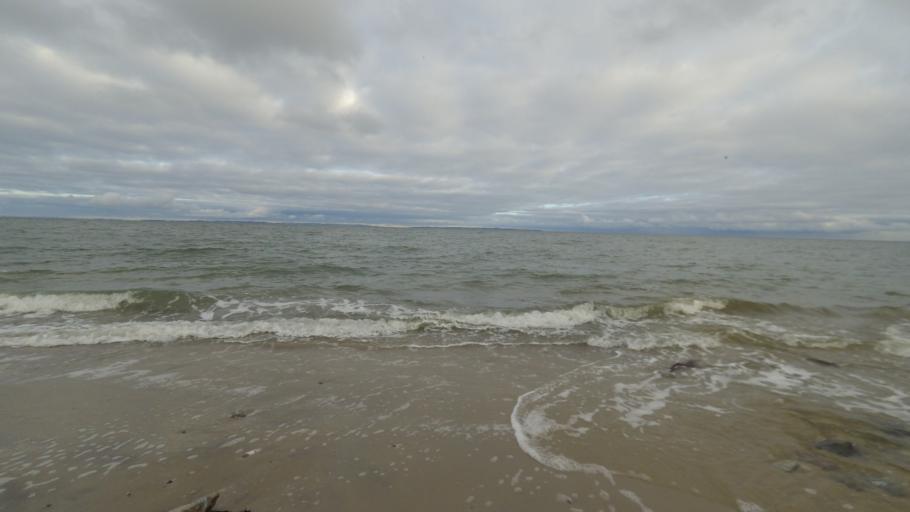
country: DK
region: Central Jutland
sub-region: Arhus Kommune
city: Beder
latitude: 56.0547
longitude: 10.2649
